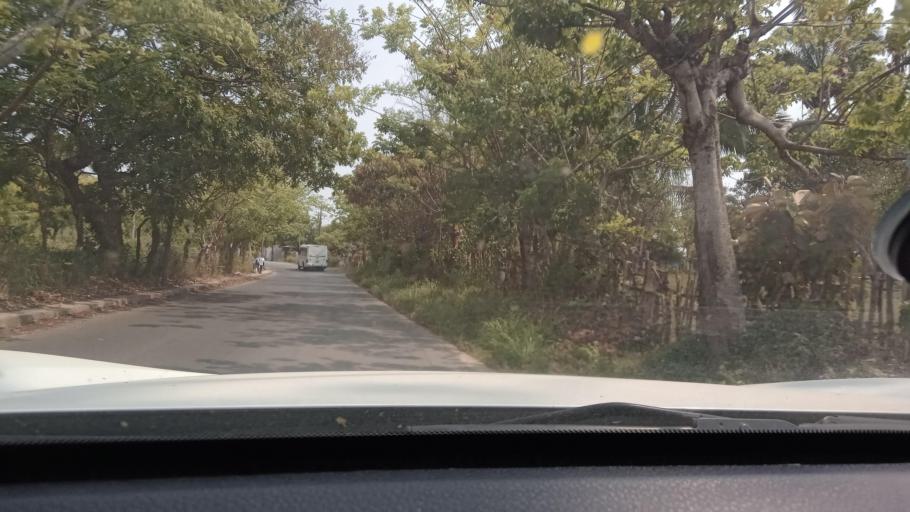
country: MX
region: Veracruz
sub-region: Minatitlan
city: Las Lomas
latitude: 17.9709
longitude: -94.5661
